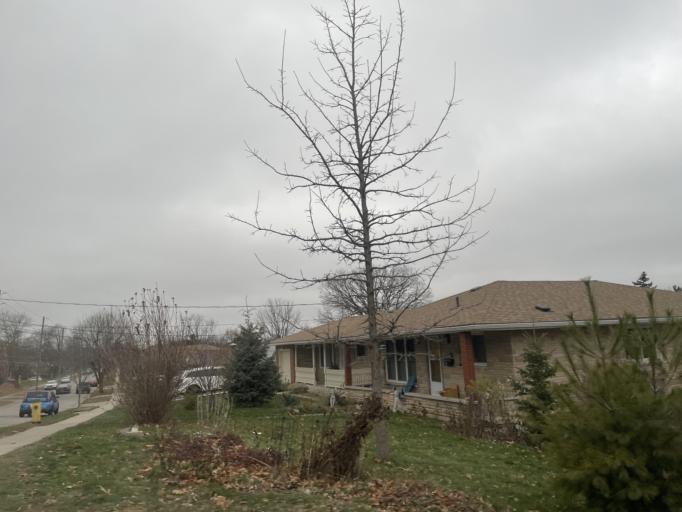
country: CA
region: Ontario
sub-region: Wellington County
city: Guelph
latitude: 43.5393
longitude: -80.2686
